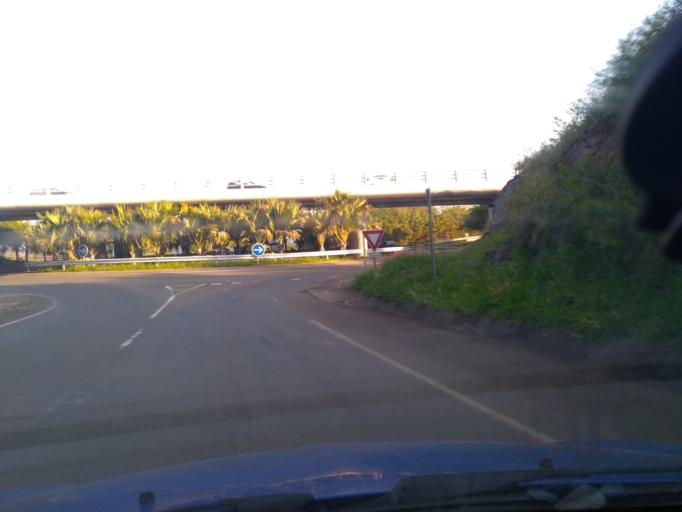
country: RE
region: Reunion
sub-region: Reunion
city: Saint-Pierre
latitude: -21.3532
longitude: 55.5161
